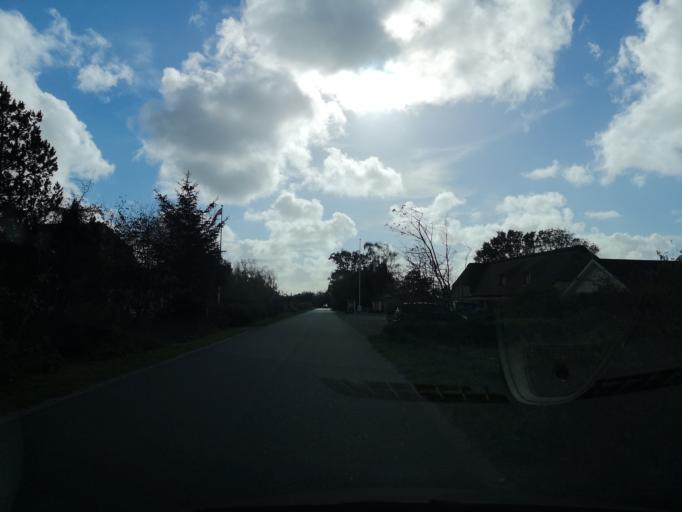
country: DK
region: South Denmark
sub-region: Varde Kommune
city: Oksbol
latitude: 55.7318
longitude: 8.2216
